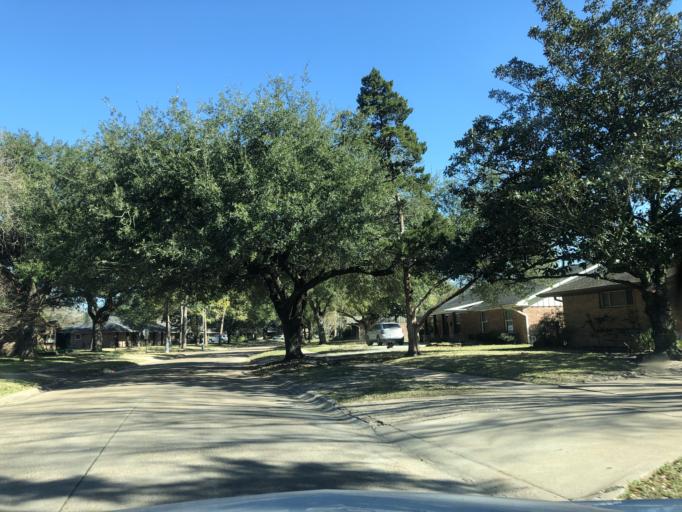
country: US
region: Texas
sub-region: Harris County
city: Bellaire
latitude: 29.6800
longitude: -95.4984
